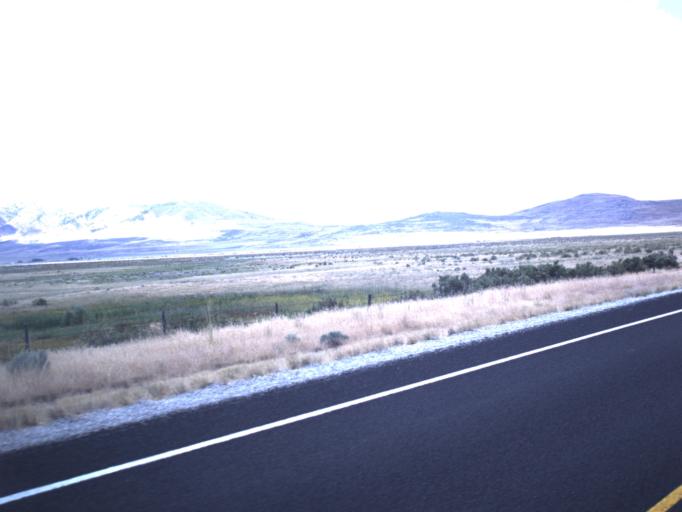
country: US
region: Utah
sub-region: Box Elder County
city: Tremonton
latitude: 41.6304
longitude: -112.4173
